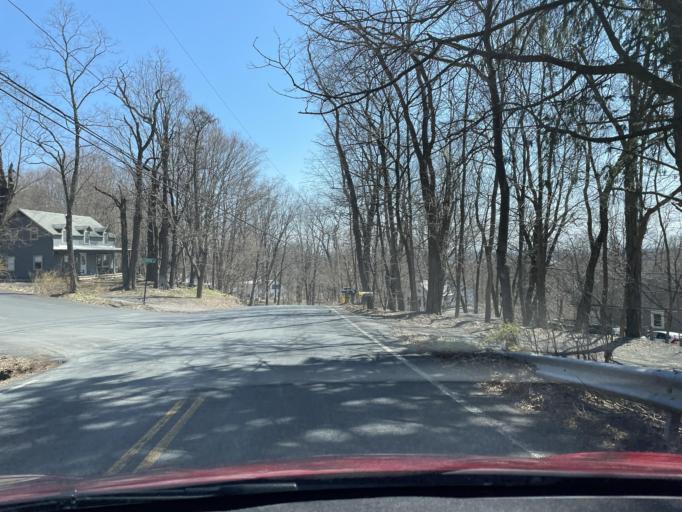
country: US
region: New York
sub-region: Ulster County
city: West Hurley
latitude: 42.0066
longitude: -74.1466
